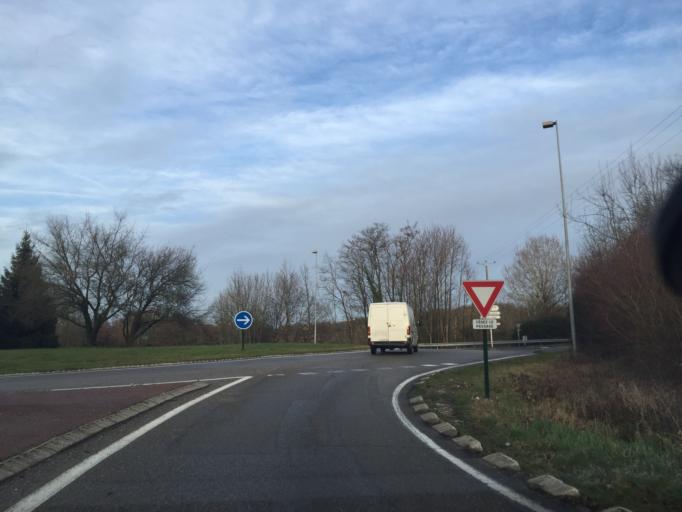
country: FR
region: Rhone-Alpes
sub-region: Departement de l'Isere
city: Vaulx-Milieu
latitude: 45.6059
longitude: 5.1654
